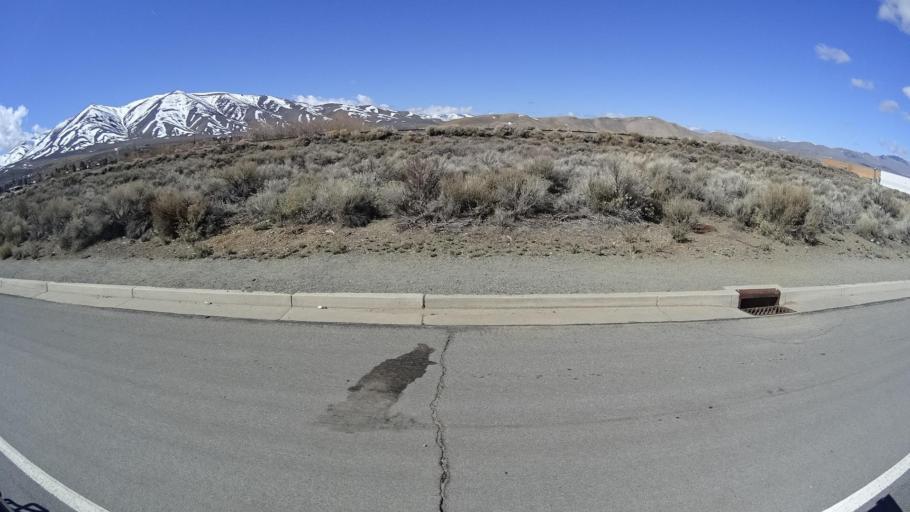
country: US
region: Nevada
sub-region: Washoe County
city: Lemmon Valley
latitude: 39.6299
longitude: -119.8823
